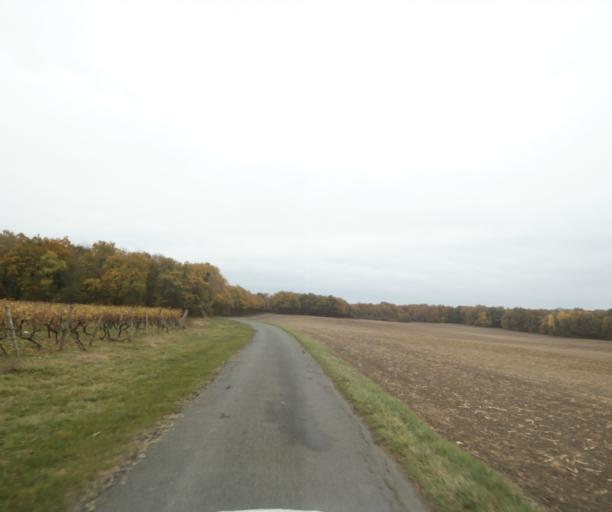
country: FR
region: Poitou-Charentes
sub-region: Departement de la Charente-Maritime
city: Chermignac
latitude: 45.7115
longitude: -0.6752
